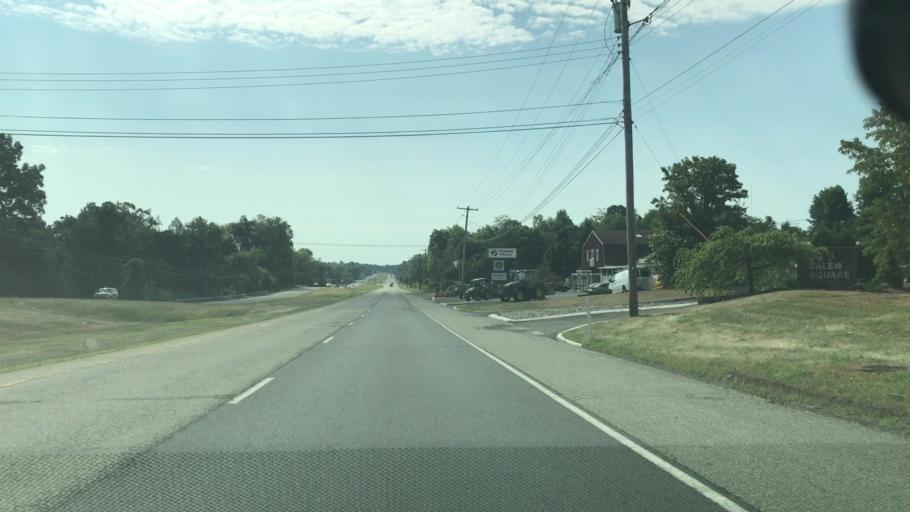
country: US
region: New Jersey
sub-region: Hunterdon County
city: Whitehouse Station
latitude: 40.6367
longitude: -74.7897
